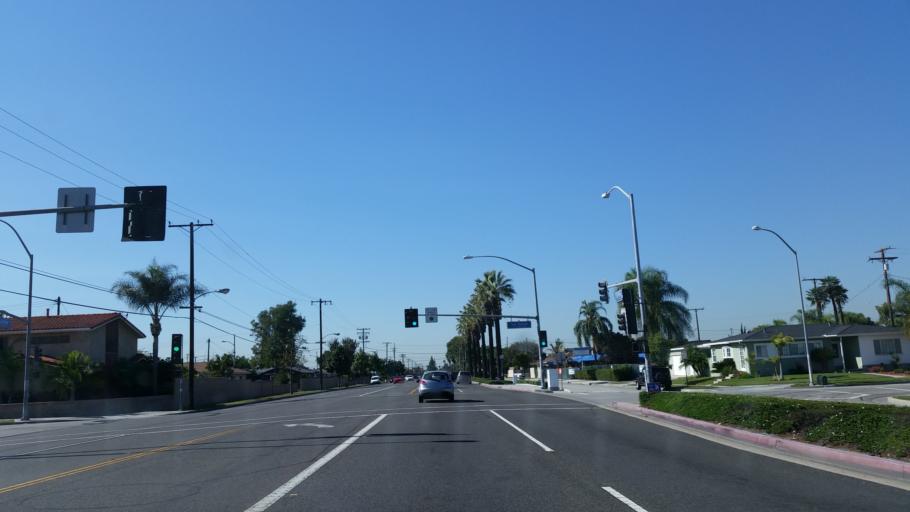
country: US
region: California
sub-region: Orange County
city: La Palma
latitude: 33.8465
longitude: -118.0236
